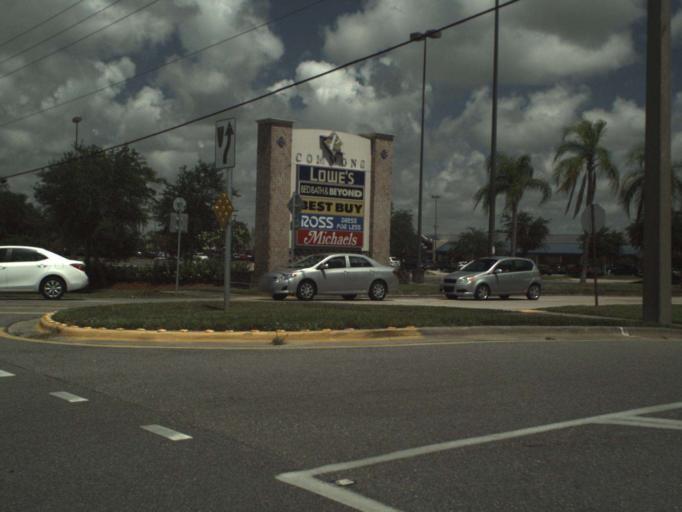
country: US
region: Florida
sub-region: Indian River County
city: West Vero Corridor
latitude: 27.6391
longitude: -80.4506
